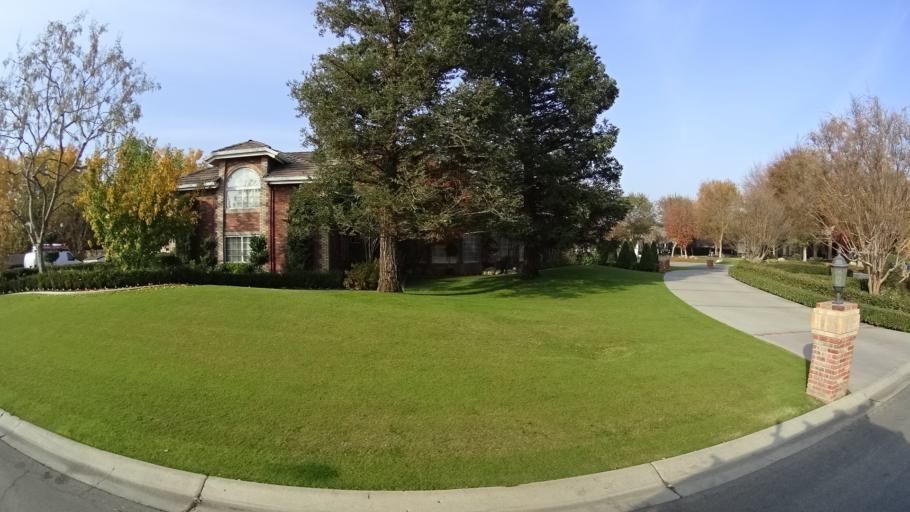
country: US
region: California
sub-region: Kern County
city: Greenacres
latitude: 35.4365
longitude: -119.1023
